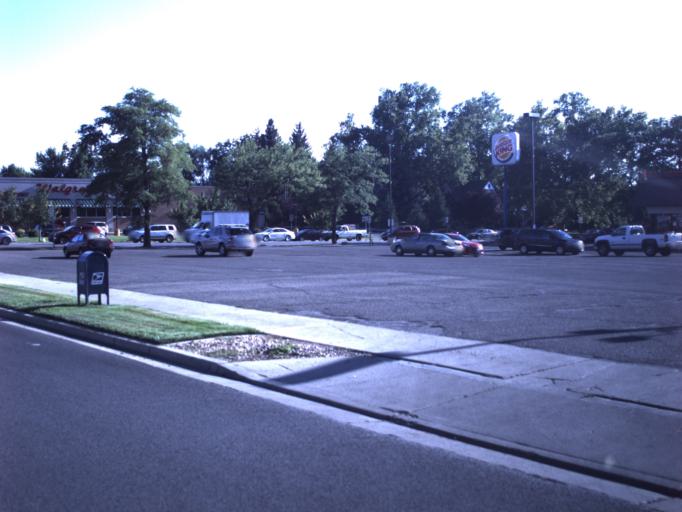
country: US
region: Utah
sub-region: Utah County
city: Springville
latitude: 40.1618
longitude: -111.6108
